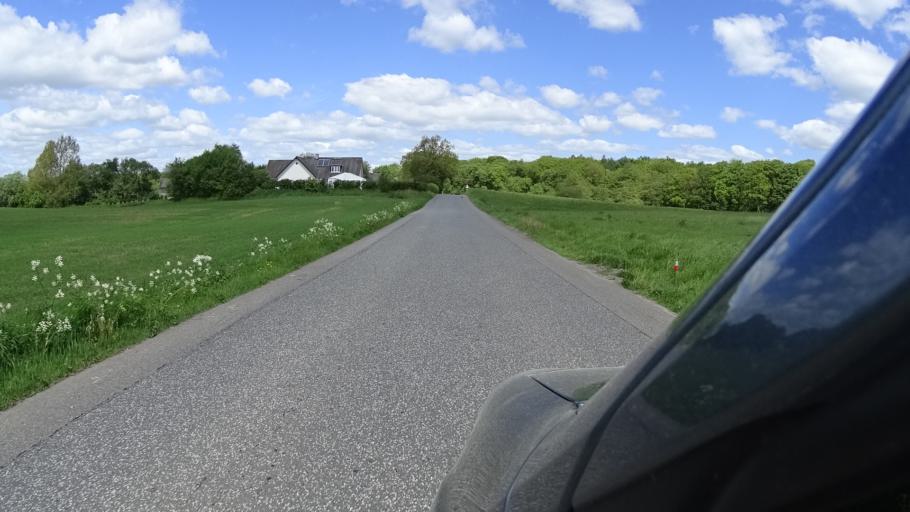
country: DK
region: South Denmark
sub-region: Vejle Kommune
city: Vejle
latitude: 55.6560
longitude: 9.5459
